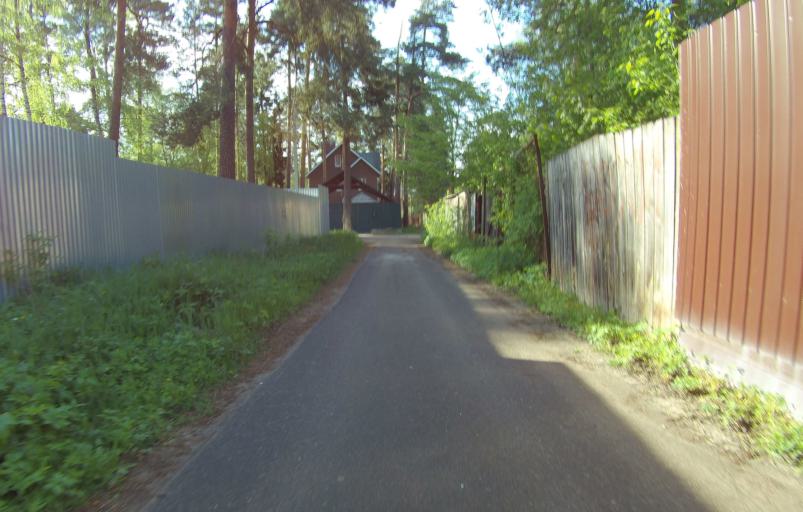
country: RU
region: Moskovskaya
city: Kratovo
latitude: 55.5939
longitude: 38.1655
